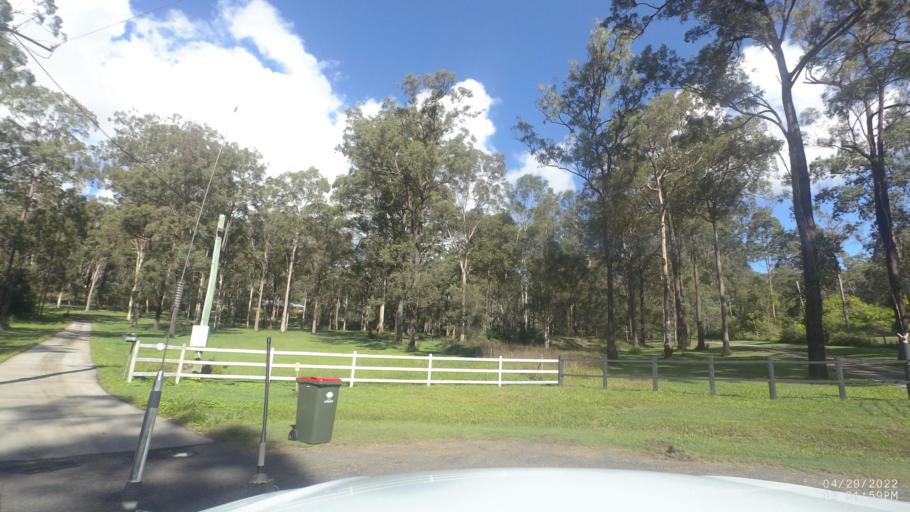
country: AU
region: Queensland
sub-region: Logan
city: Windaroo
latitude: -27.7961
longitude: 153.1490
